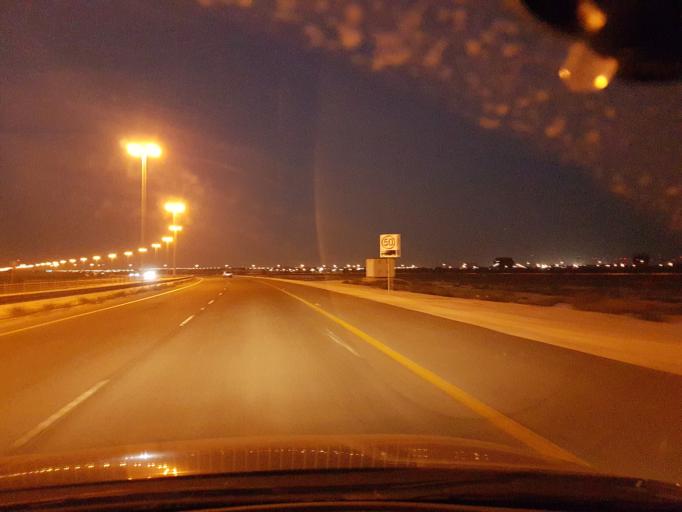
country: BH
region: Central Governorate
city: Dar Kulayb
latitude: 26.0300
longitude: 50.4988
